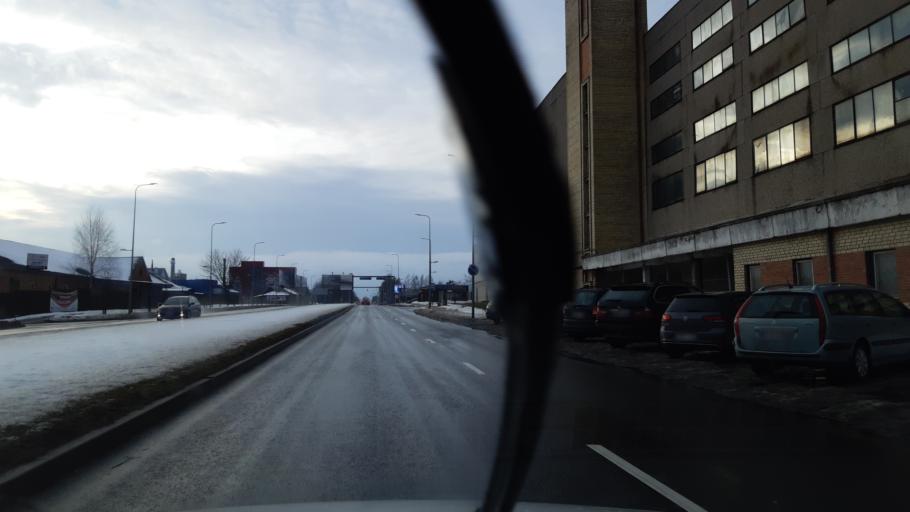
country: LT
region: Kauno apskritis
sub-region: Kaunas
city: Aleksotas
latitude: 54.8752
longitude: 23.8959
